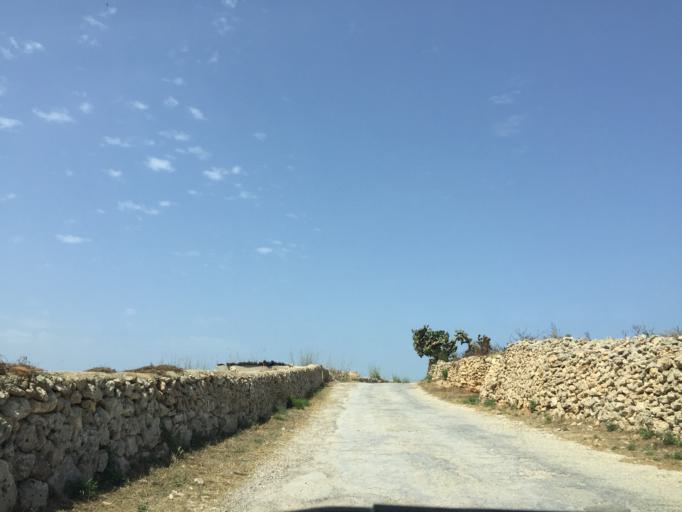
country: MT
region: In-Nadur
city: Nadur
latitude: 36.0539
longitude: 14.2941
